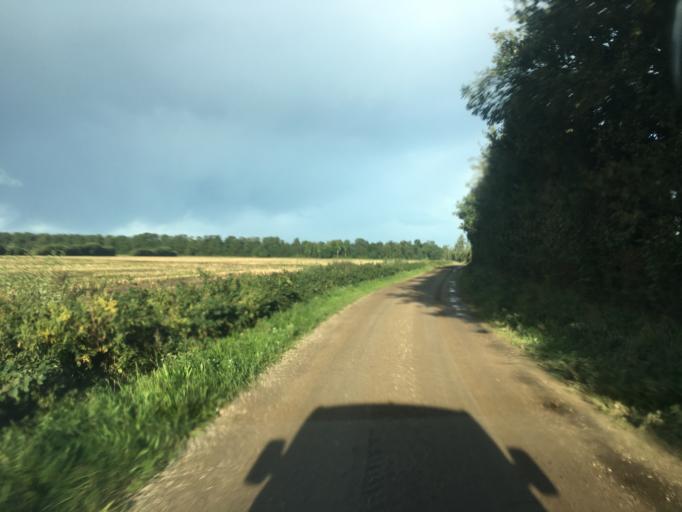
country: DE
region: Schleswig-Holstein
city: Ellhoft
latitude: 54.9628
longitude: 8.9840
